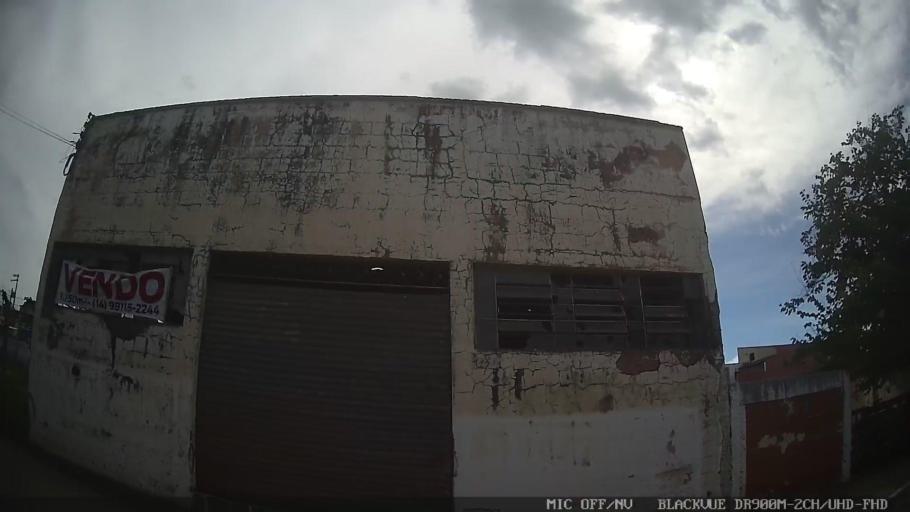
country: BR
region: Sao Paulo
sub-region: Conchas
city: Conchas
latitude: -23.0157
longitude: -48.0036
